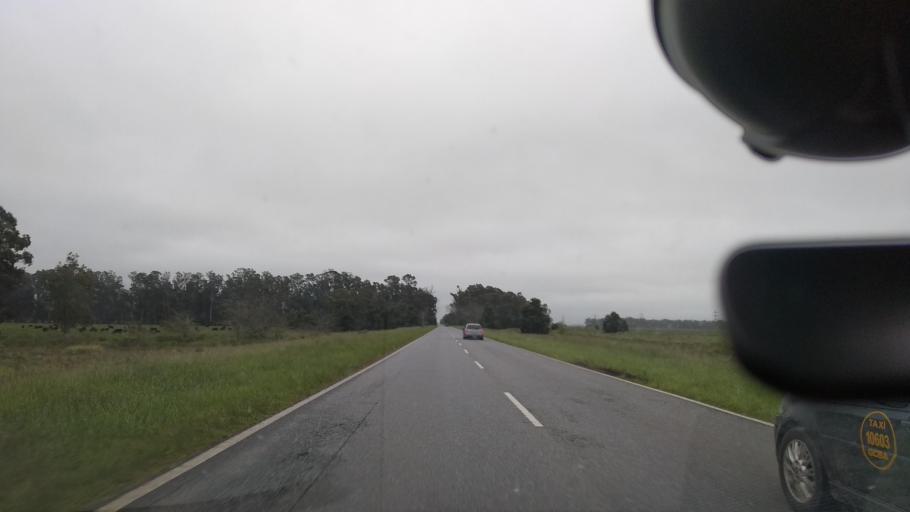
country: AR
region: Buenos Aires
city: Veronica
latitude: -35.3202
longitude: -57.4779
